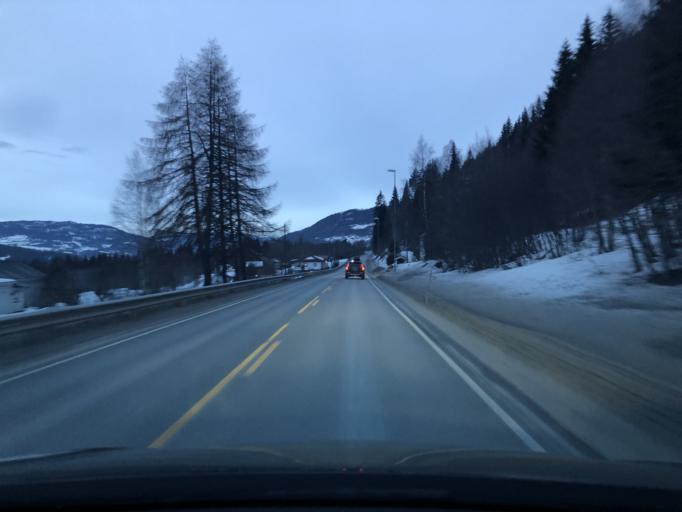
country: NO
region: Oppland
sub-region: Sor-Aurdal
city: Bagn
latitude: 60.9002
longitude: 9.4514
